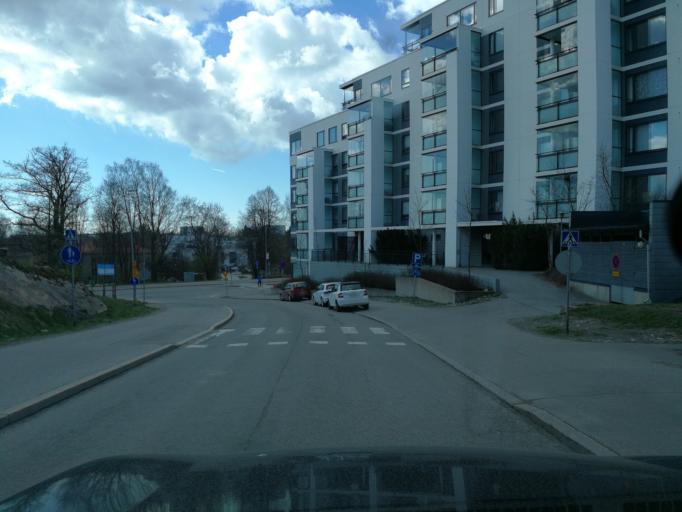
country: FI
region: Uusimaa
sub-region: Helsinki
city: Koukkuniemi
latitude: 60.1628
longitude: 24.7482
